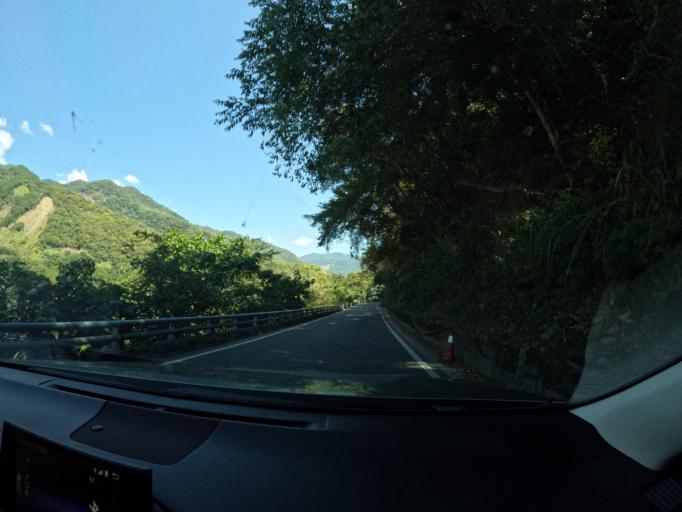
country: TW
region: Taiwan
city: Yujing
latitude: 23.2440
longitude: 120.8142
